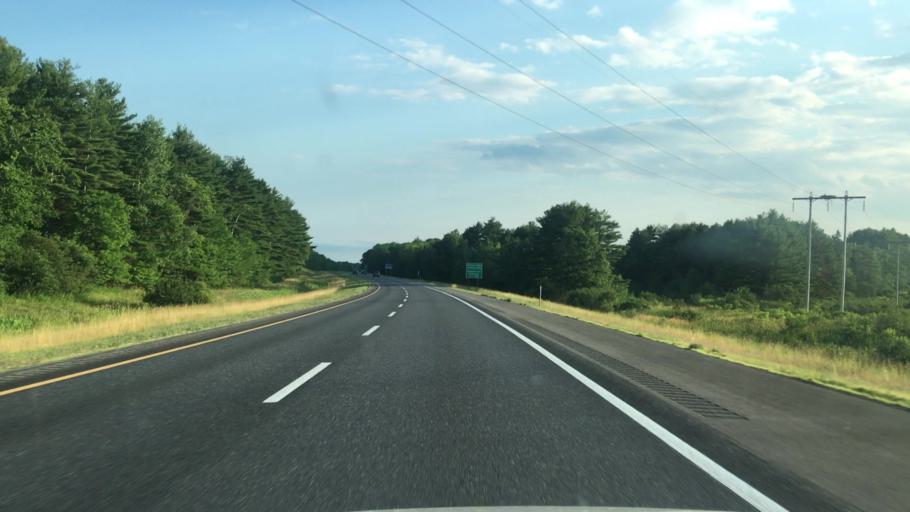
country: US
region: Maine
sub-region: Sagadahoc County
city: Topsham
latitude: 43.9673
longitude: -69.9558
